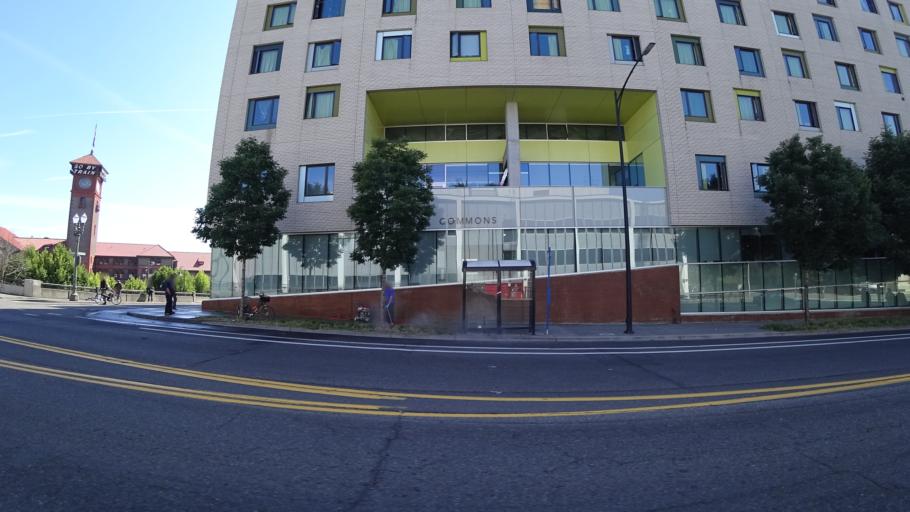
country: US
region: Oregon
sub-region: Multnomah County
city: Portland
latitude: 45.5279
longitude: -122.6777
